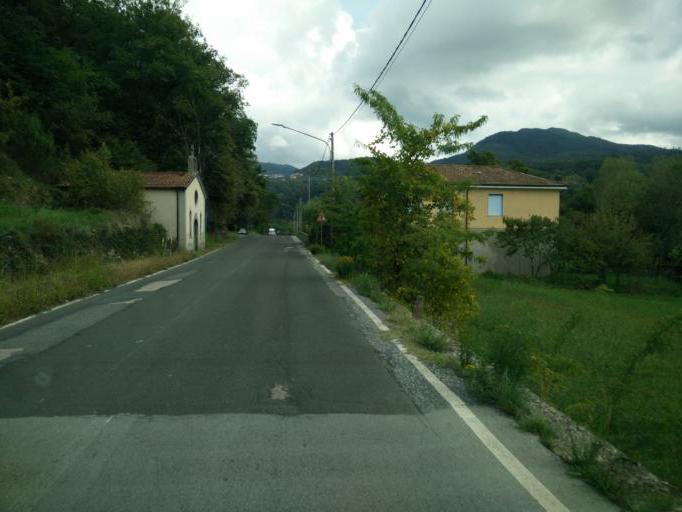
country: IT
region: Tuscany
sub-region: Provincia di Massa-Carrara
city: Bagnone
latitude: 44.3112
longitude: 9.9830
